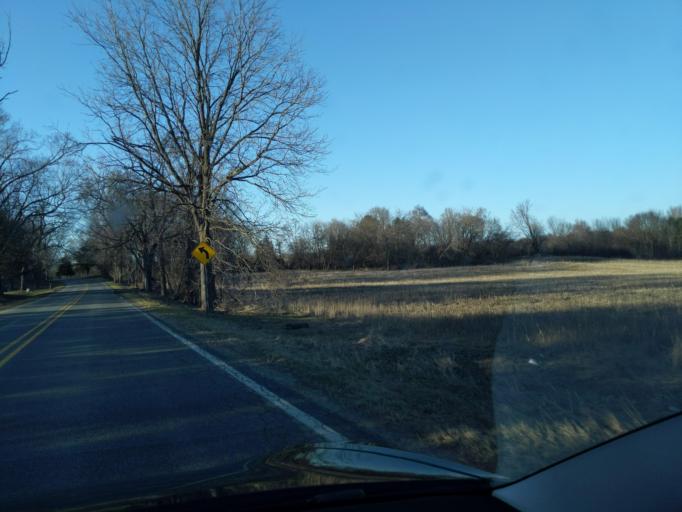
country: US
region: Michigan
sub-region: Washtenaw County
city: Chelsea
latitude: 42.4219
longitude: -84.0538
